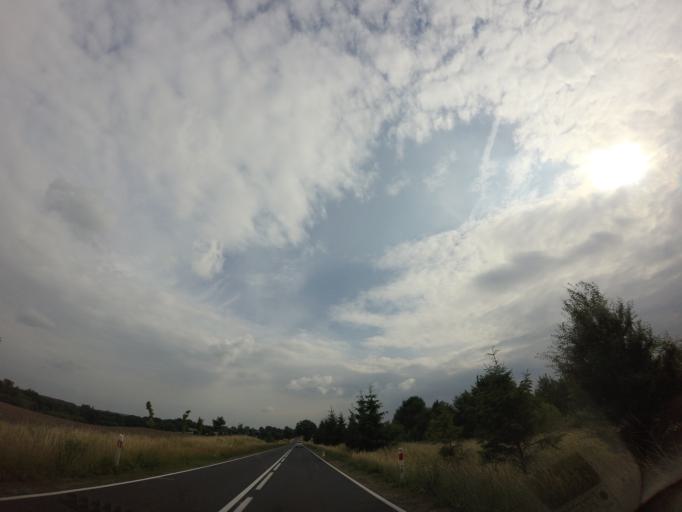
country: PL
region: West Pomeranian Voivodeship
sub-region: Powiat szczecinecki
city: Szczecinek
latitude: 53.6708
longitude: 16.6795
